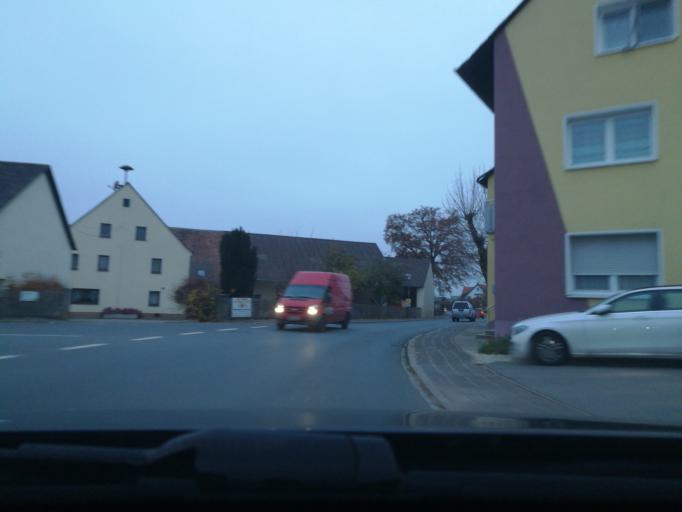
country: DE
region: Bavaria
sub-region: Regierungsbezirk Mittelfranken
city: Obermichelbach
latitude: 49.5145
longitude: 10.9255
